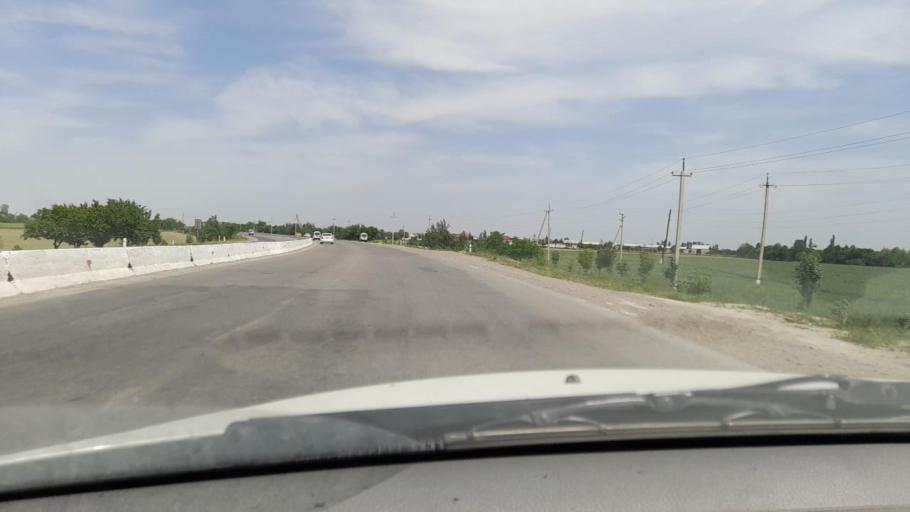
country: UZ
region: Bukhara
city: Wobkent
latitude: 40.0319
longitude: 64.5388
